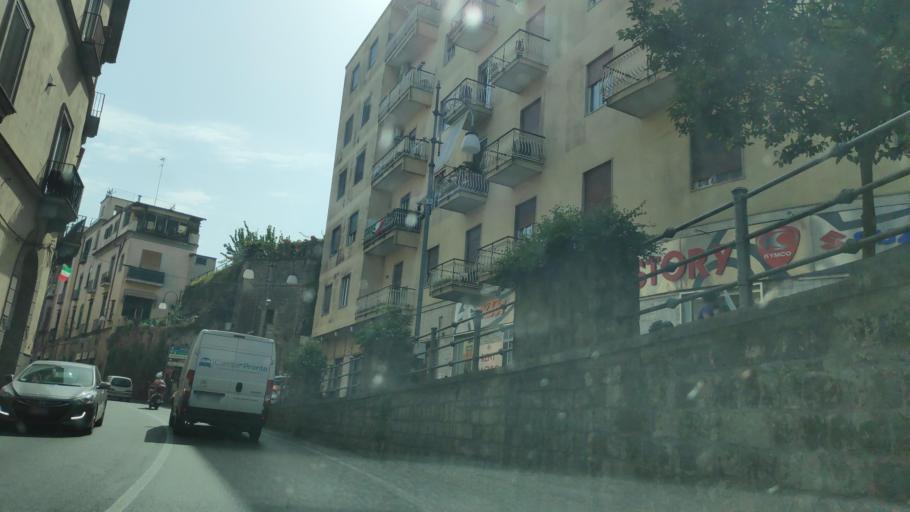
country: IT
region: Campania
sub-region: Provincia di Napoli
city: Sant'Agnello
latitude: 40.6300
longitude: 14.4007
